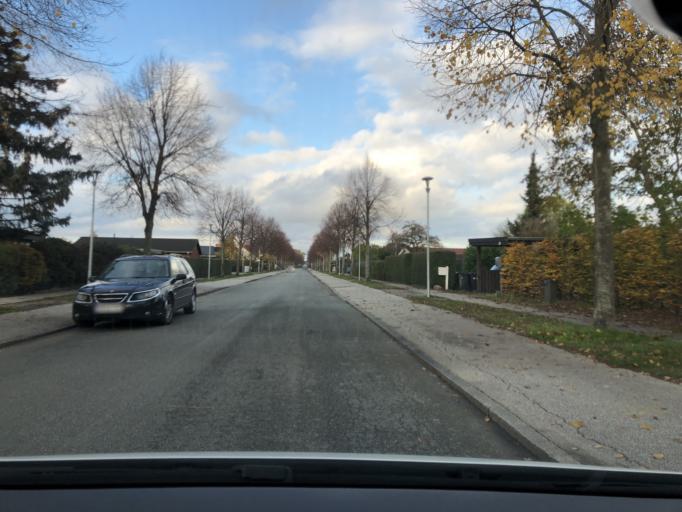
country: DK
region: Capital Region
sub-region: Tarnby Kommune
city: Tarnby
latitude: 55.6174
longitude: 12.5979
